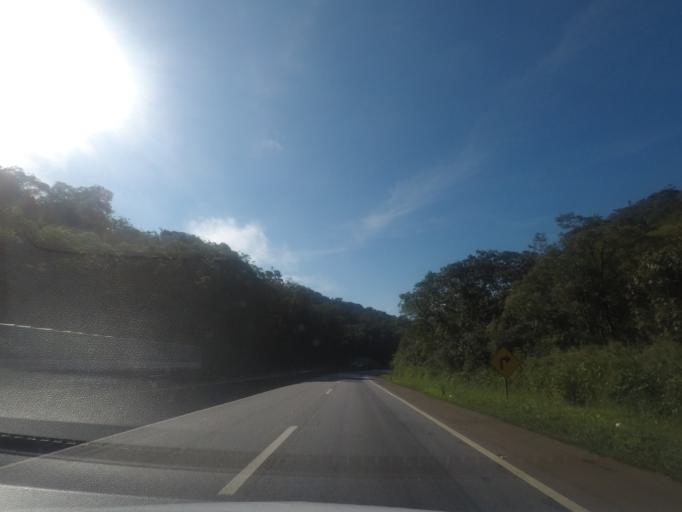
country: BR
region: Parana
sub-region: Piraquara
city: Piraquara
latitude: -25.5933
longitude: -48.9102
